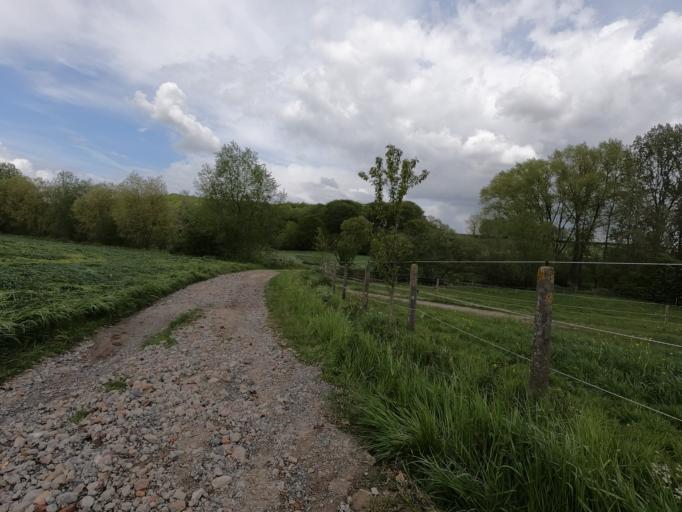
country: BE
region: Flanders
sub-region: Provincie Oost-Vlaanderen
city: Ronse
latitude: 50.7811
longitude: 3.5813
